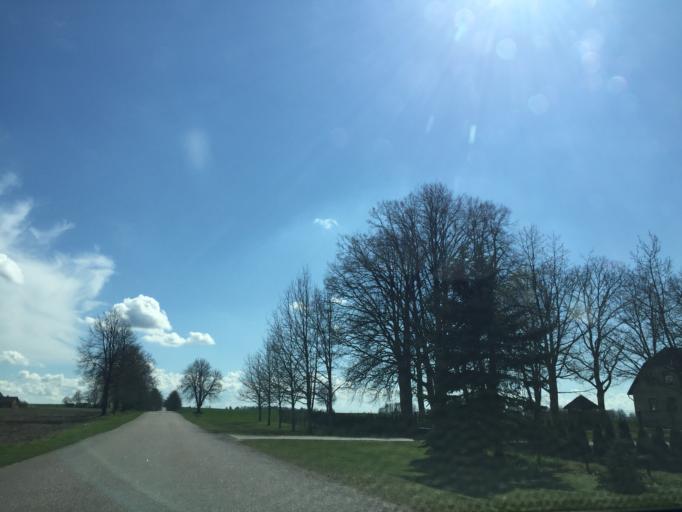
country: LV
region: Strenci
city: Strenci
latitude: 57.5608
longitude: 25.7141
